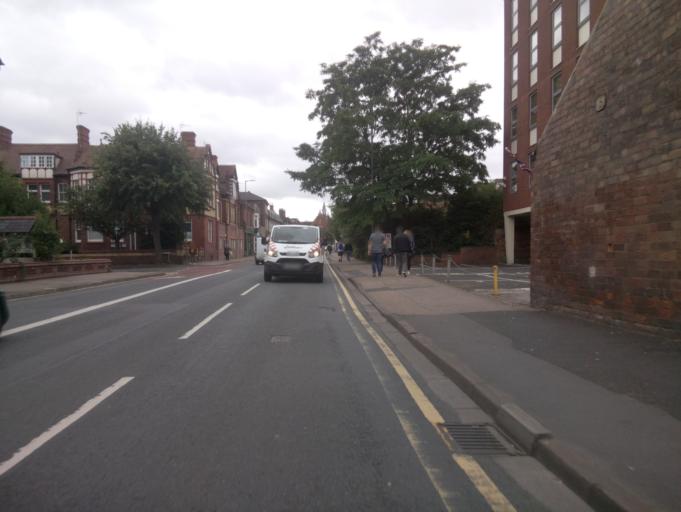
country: GB
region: England
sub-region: Worcestershire
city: Worcester
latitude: 52.2025
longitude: -2.2261
